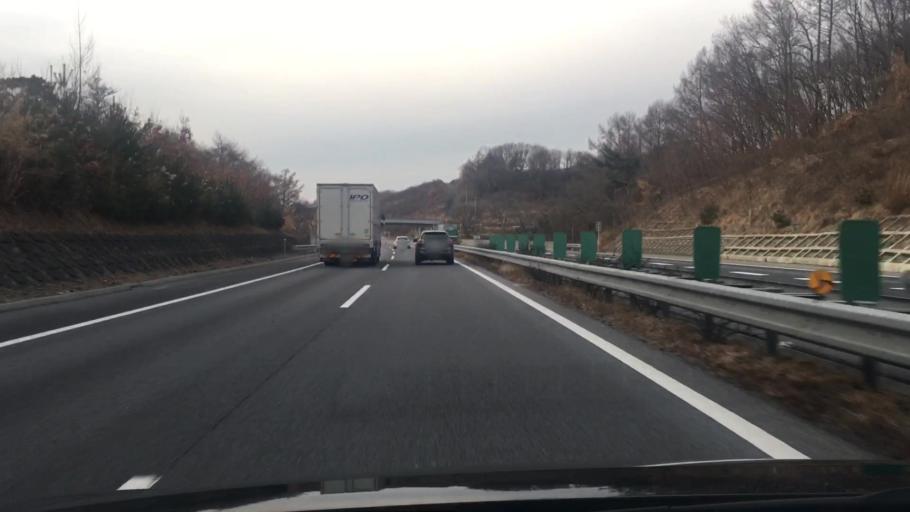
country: JP
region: Nagano
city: Komoro
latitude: 36.3402
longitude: 138.4374
